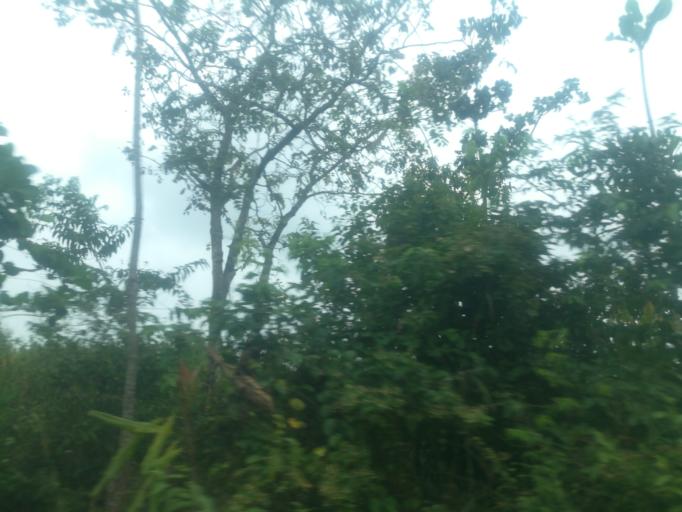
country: NG
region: Ogun
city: Ayetoro
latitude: 7.1043
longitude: 3.1456
